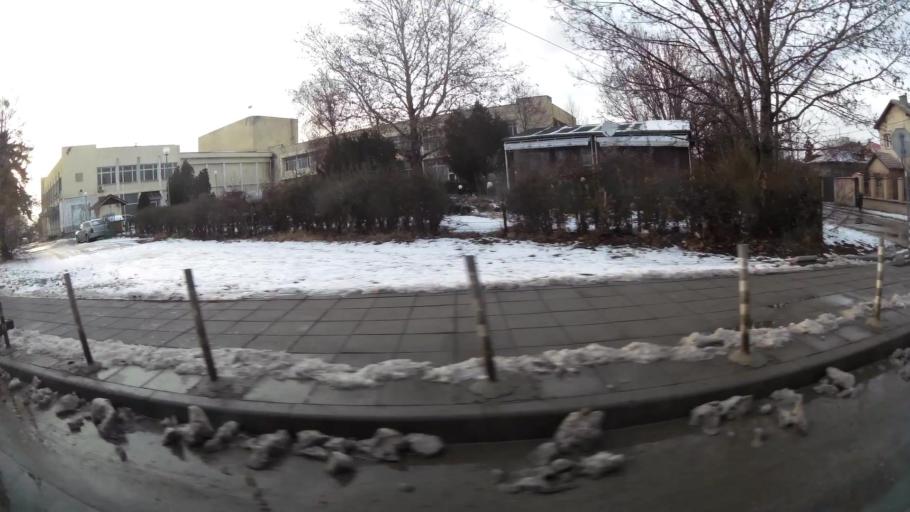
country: BG
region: Sofia-Capital
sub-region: Stolichna Obshtina
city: Sofia
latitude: 42.7232
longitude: 23.3431
